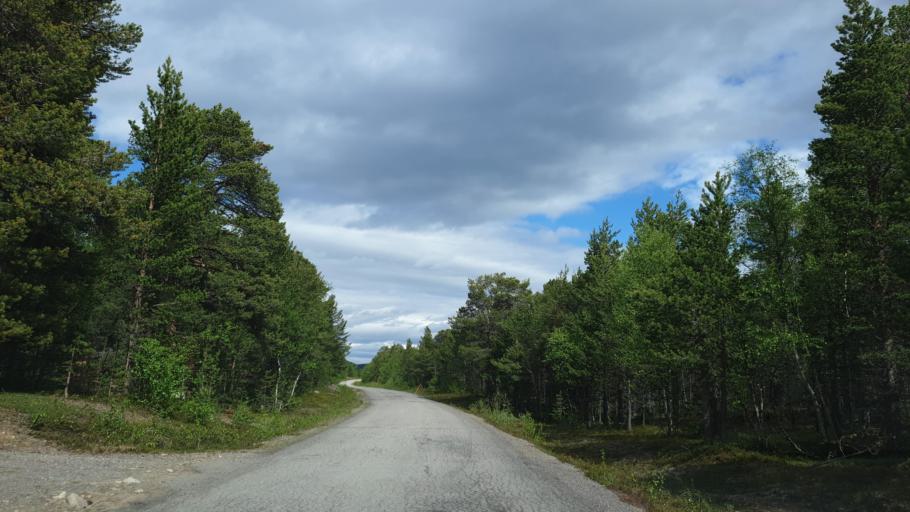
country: SE
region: Norrbotten
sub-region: Kiruna Kommun
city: Kiruna
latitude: 68.2224
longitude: 19.7141
